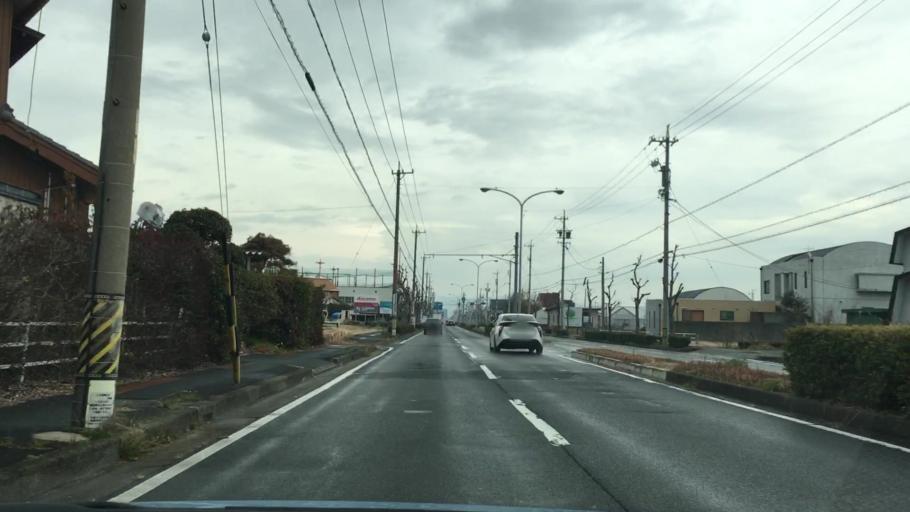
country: JP
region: Aichi
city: Toyohashi
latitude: 34.7651
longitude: 137.3550
